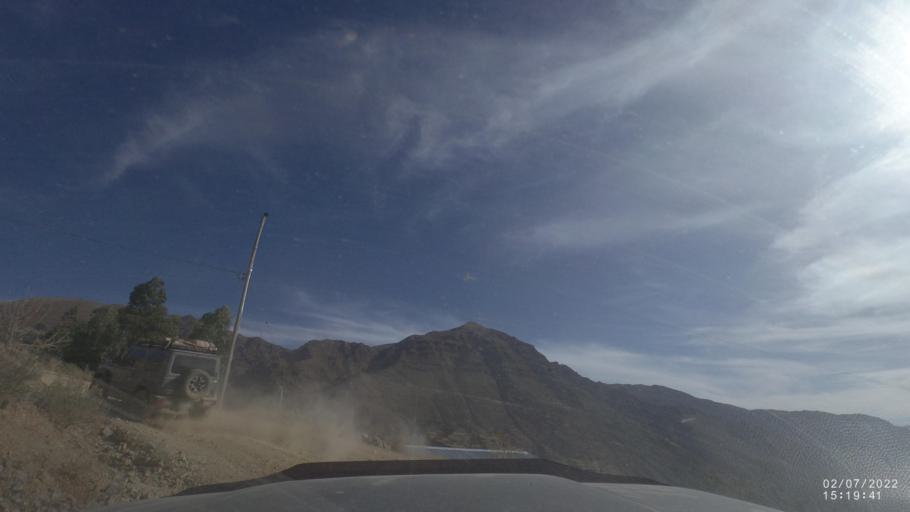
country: BO
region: Cochabamba
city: Irpa Irpa
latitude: -17.8678
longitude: -66.4288
